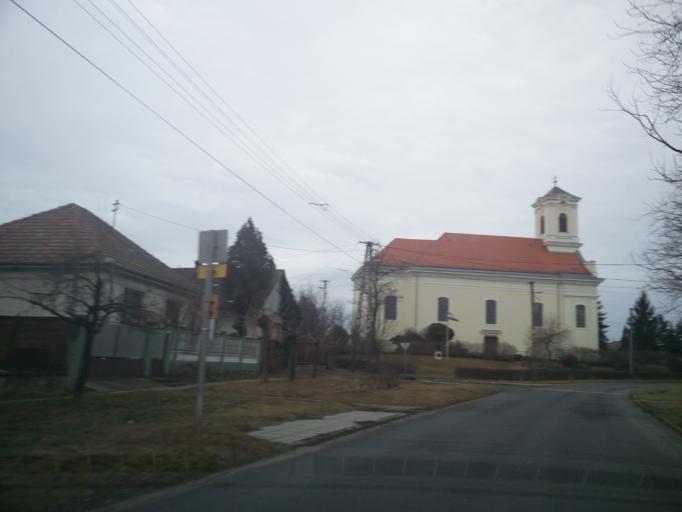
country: HU
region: Pest
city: Koka
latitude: 47.4898
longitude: 19.5744
